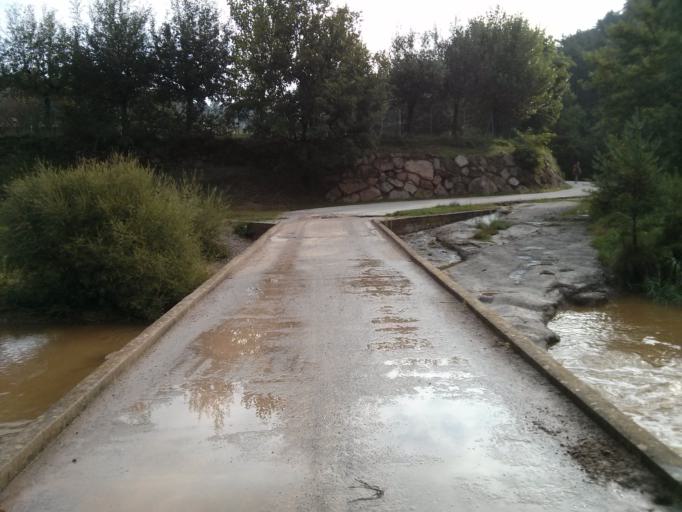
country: ES
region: Catalonia
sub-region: Provincia de Barcelona
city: Borreda
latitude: 42.0915
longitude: 2.0075
